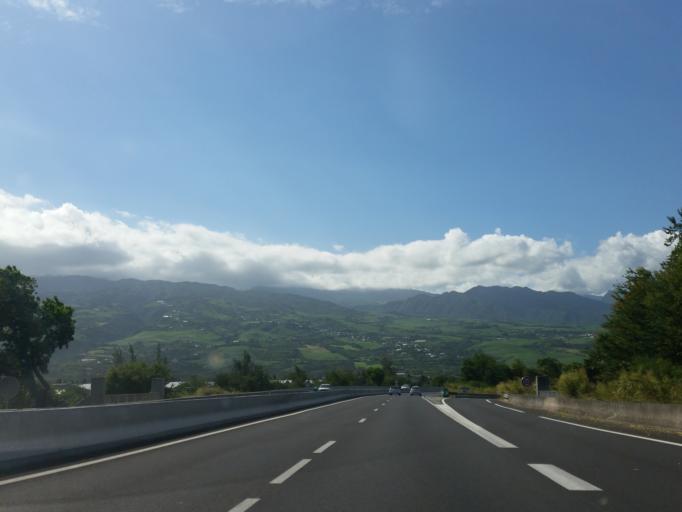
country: RE
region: Reunion
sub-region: Reunion
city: Saint-Louis
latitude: -21.2816
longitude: 55.3773
